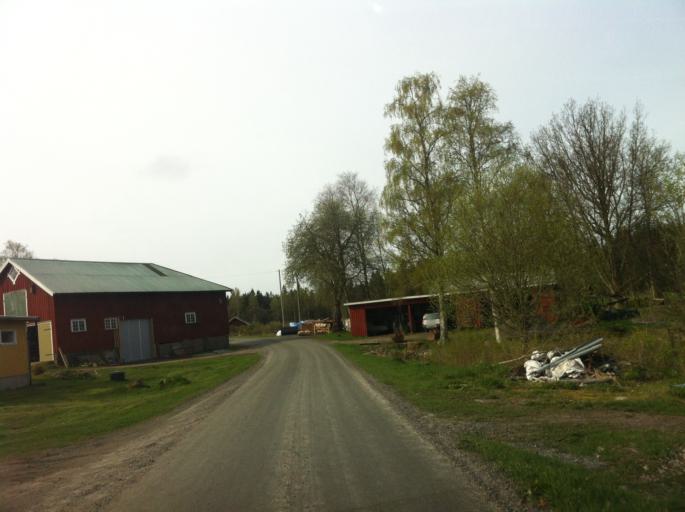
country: SE
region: Vaestra Goetaland
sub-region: Bollebygds Kommun
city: Bollebygd
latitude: 57.7628
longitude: 12.5843
